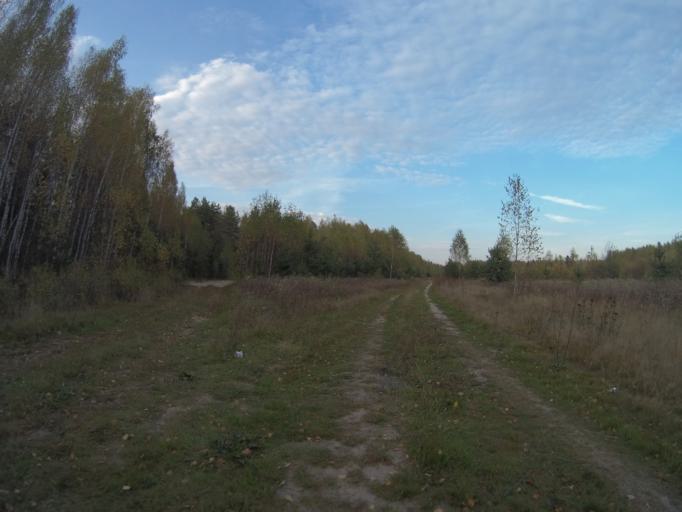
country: RU
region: Vladimir
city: Sobinka
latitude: 55.8581
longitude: 40.0901
